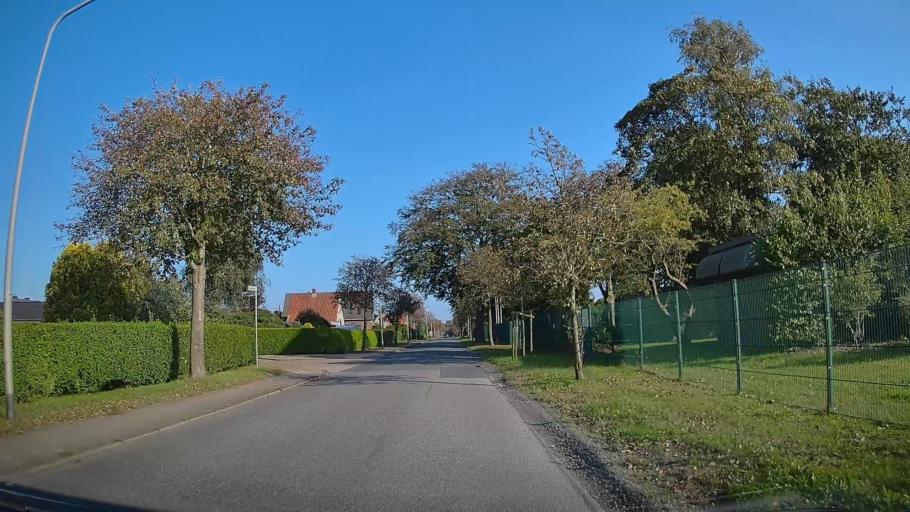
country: DE
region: Lower Saxony
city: Cuxhaven
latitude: 53.8505
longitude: 8.6653
